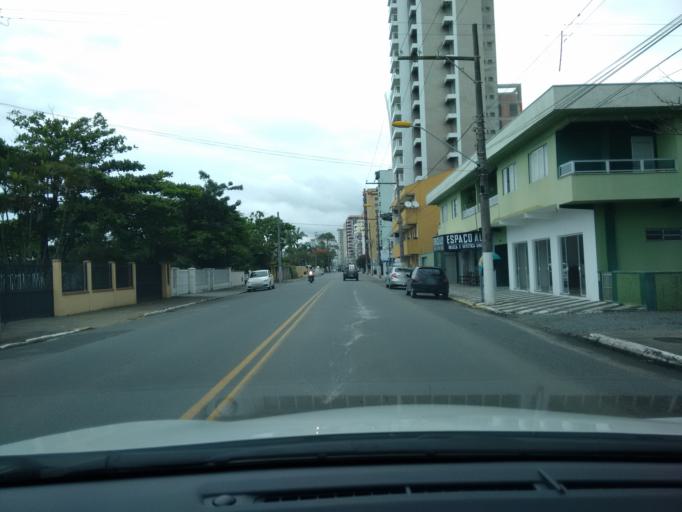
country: BR
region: Santa Catarina
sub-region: Penha
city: Penha
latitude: -26.7536
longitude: -48.6769
